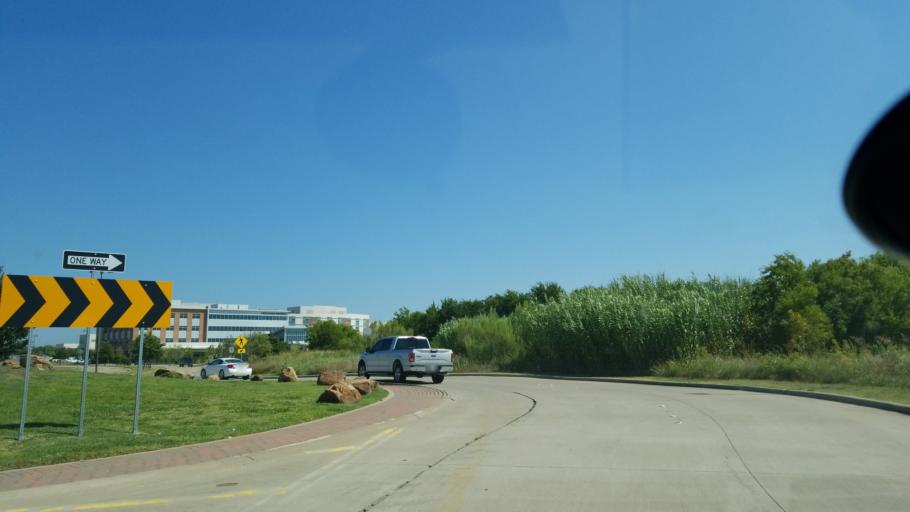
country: US
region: Texas
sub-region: Tarrant County
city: Mansfield
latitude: 32.5636
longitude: -97.0951
